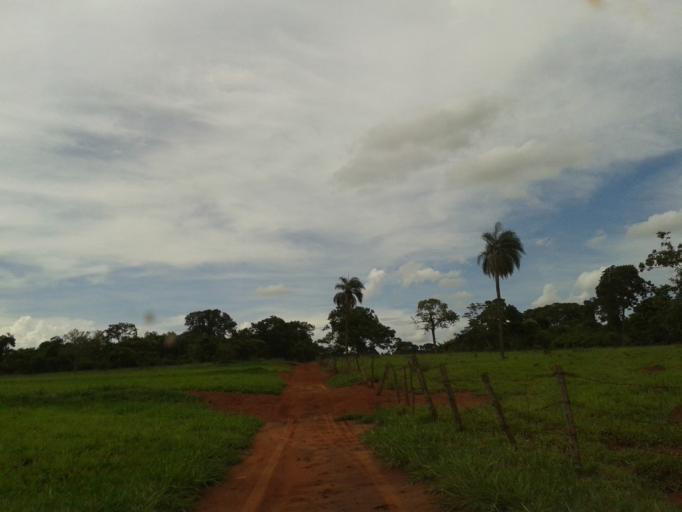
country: BR
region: Minas Gerais
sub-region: Santa Vitoria
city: Santa Vitoria
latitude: -18.7979
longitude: -49.8507
